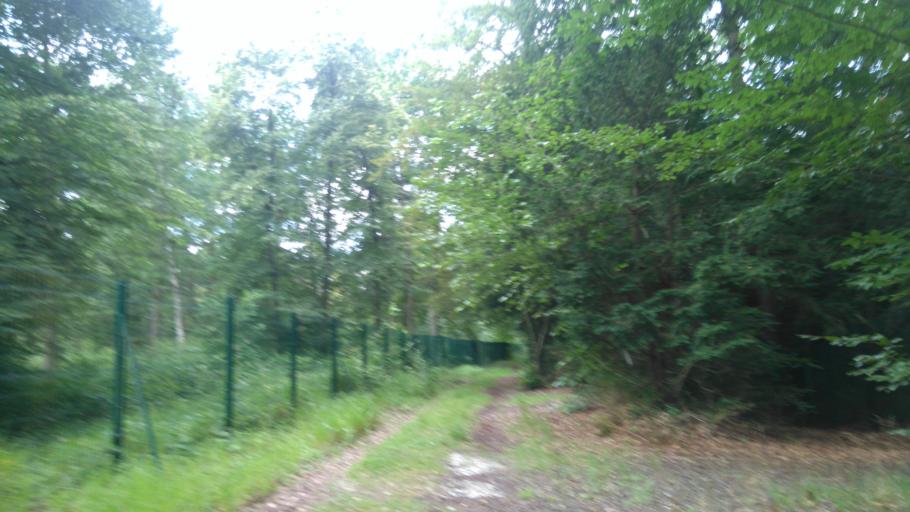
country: FR
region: Picardie
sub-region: Departement de l'Oise
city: Saint-Maximin
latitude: 49.2335
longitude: 2.4538
